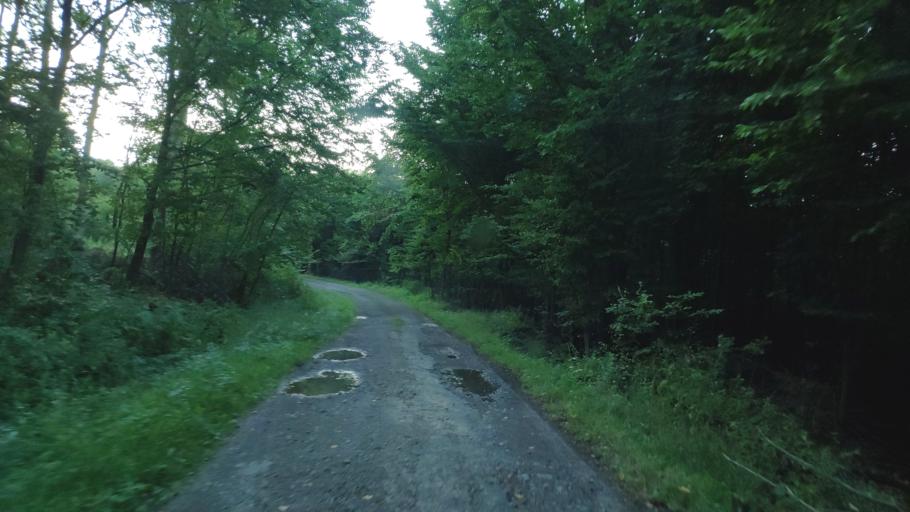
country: SK
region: Kosicky
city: Secovce
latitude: 48.5881
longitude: 21.5284
